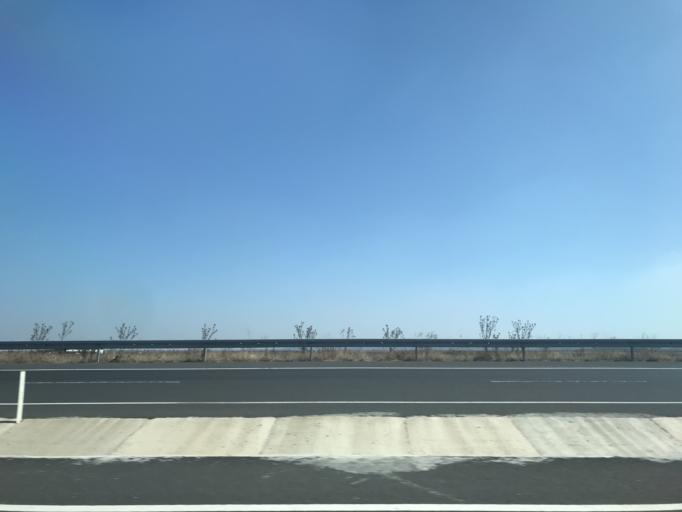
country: TR
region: Tekirdag
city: Muratli
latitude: 41.1727
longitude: 27.5376
